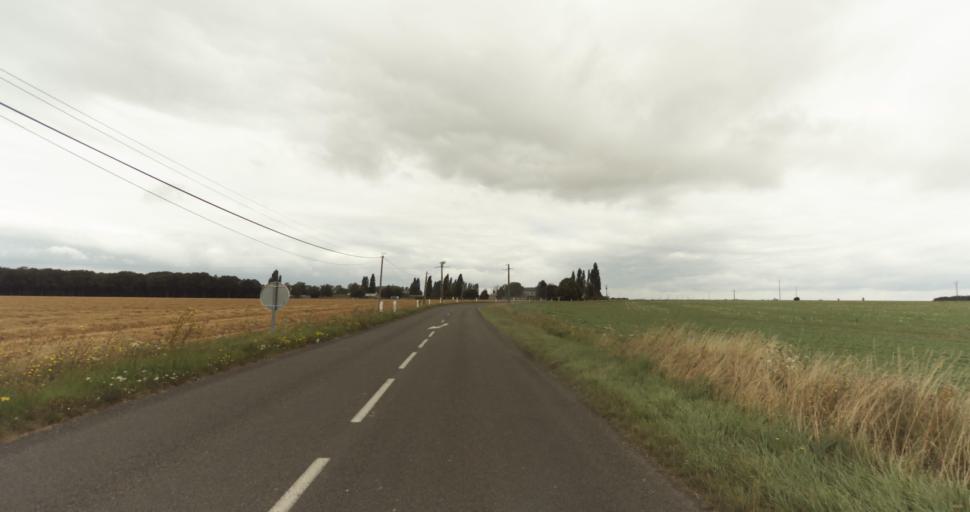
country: FR
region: Haute-Normandie
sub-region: Departement de l'Eure
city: Gravigny
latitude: 49.0413
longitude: 1.2108
